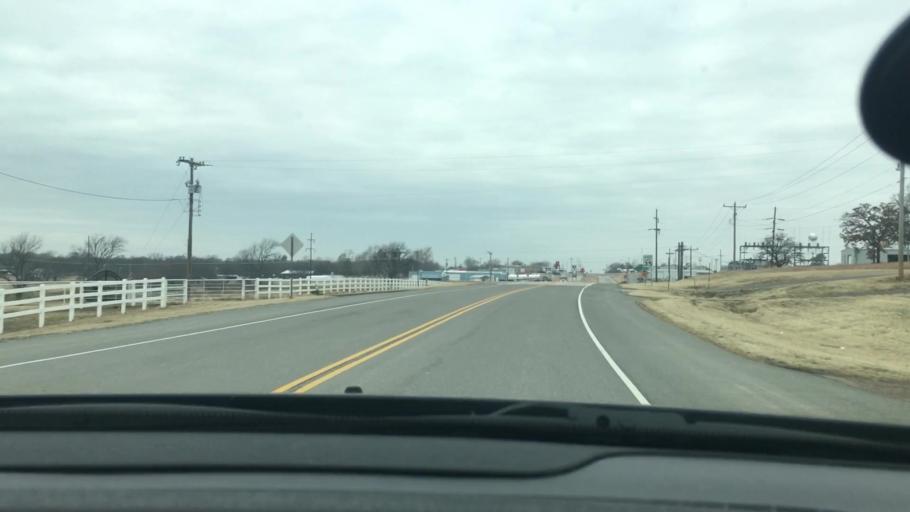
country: US
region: Oklahoma
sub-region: Carter County
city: Healdton
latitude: 34.4489
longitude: -97.5056
